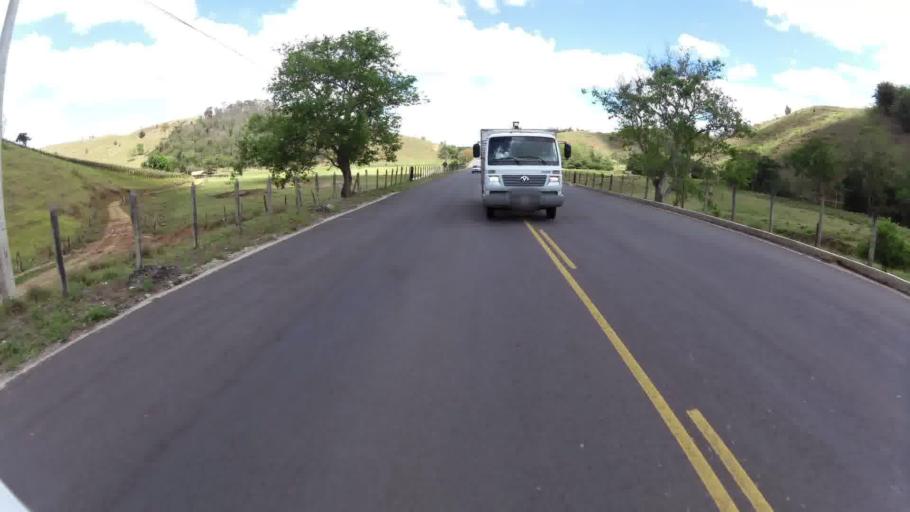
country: BR
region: Rio de Janeiro
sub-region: Cambuci
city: Cambuci
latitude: -21.3918
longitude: -41.9710
